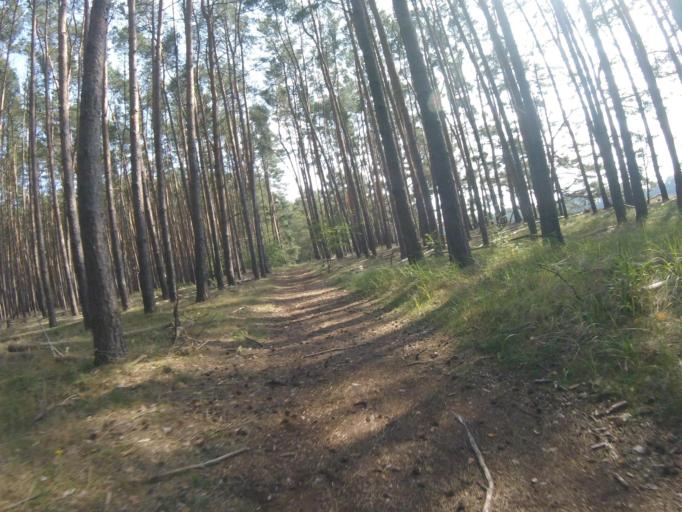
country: DE
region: Brandenburg
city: Bestensee
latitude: 52.2544
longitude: 13.7595
